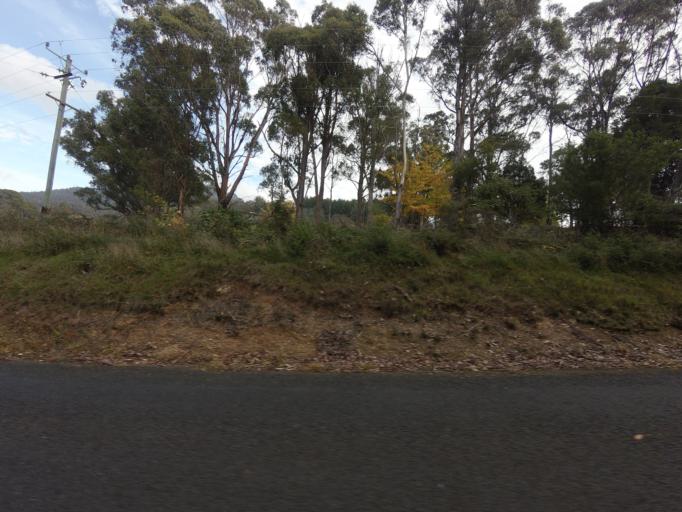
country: AU
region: Tasmania
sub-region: Meander Valley
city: Deloraine
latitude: -41.6225
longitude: 146.7041
